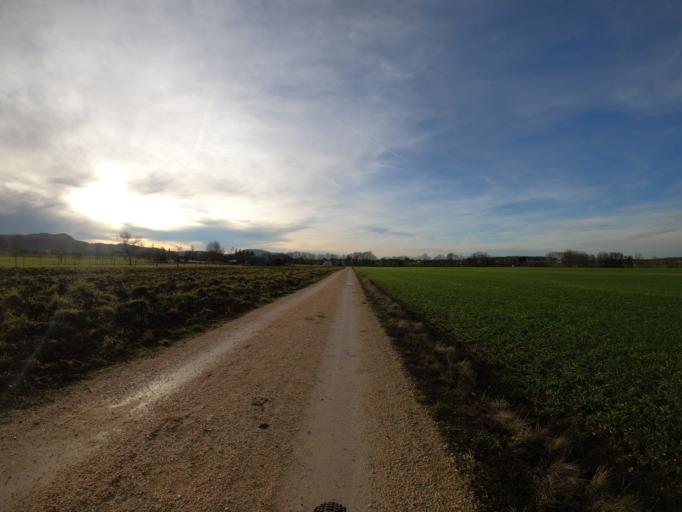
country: DE
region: Baden-Wuerttemberg
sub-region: Regierungsbezirk Stuttgart
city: Durnau
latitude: 48.6505
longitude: 9.6277
